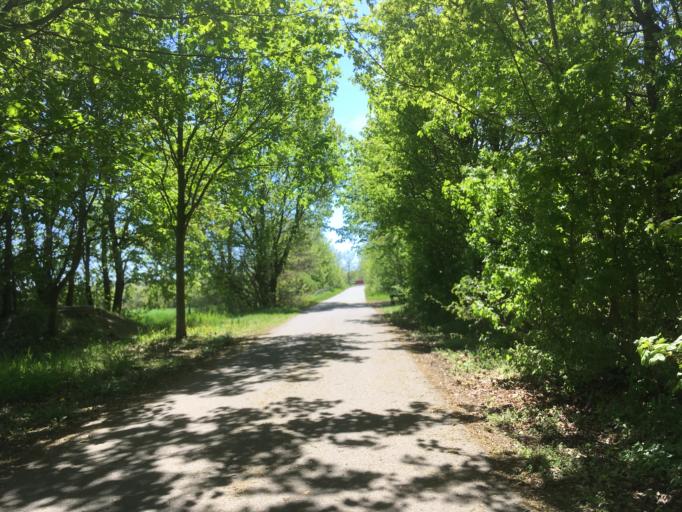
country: DE
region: Brandenburg
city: Wildau
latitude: 52.3127
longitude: 13.6155
